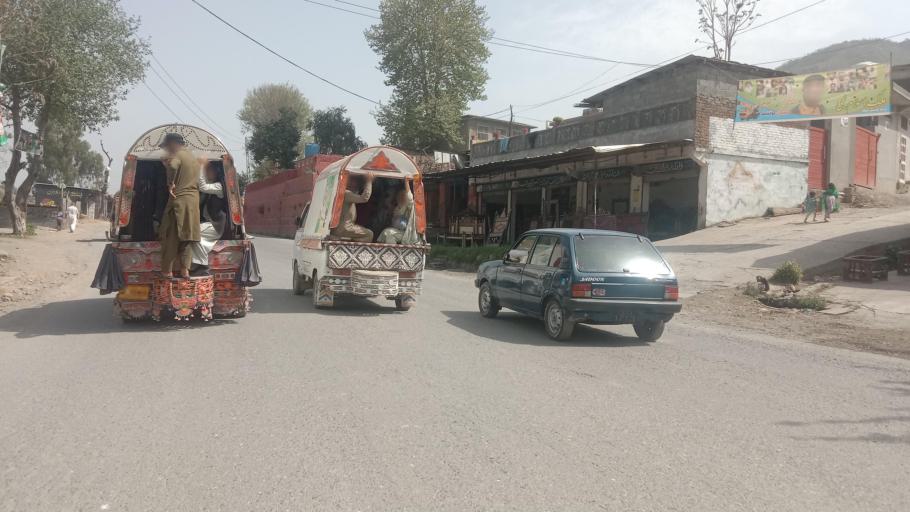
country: PK
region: Khyber Pakhtunkhwa
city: Abbottabad
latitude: 34.1261
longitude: 73.1936
